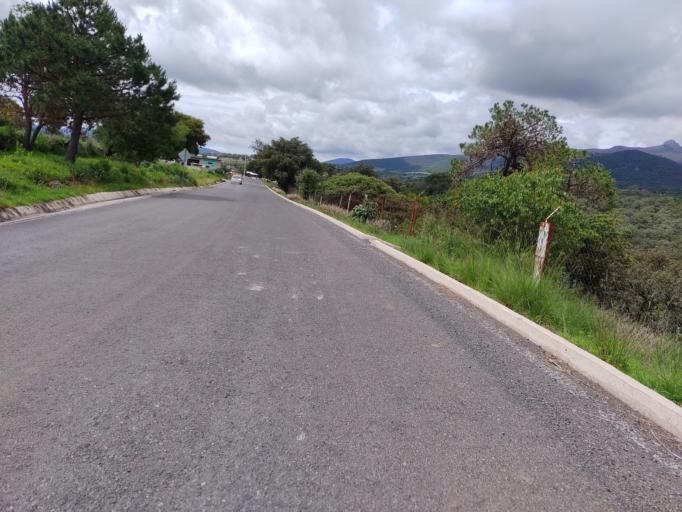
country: MX
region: Mexico
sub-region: Aculco
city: Gunyo Poniente (San Jose Gunyo)
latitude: 20.1155
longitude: -99.8804
